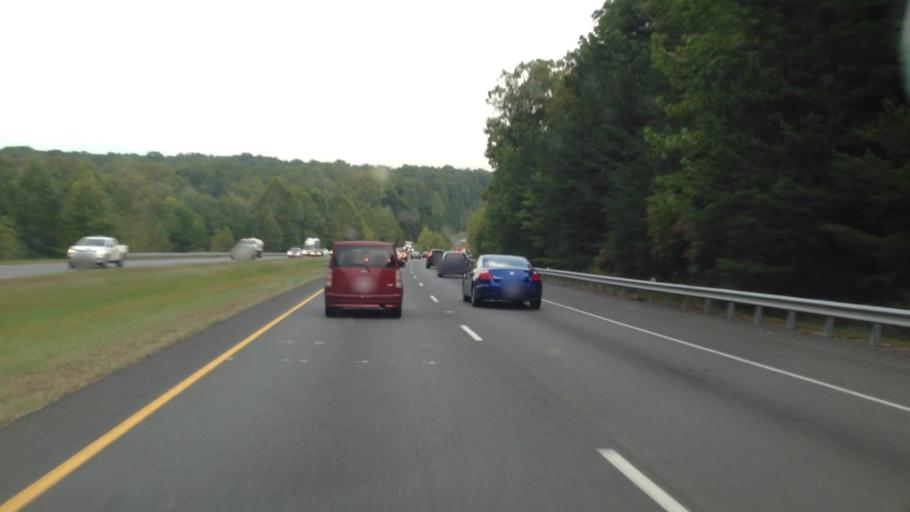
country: US
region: Virginia
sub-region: Fairfax County
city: Fairfax Station
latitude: 38.8010
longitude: -77.3414
